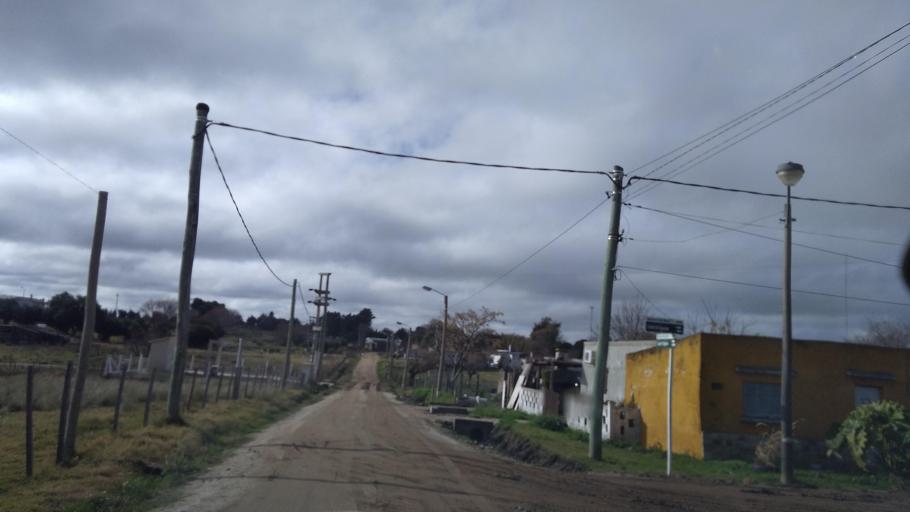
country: UY
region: Canelones
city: Tala
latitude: -34.1907
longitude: -55.7419
